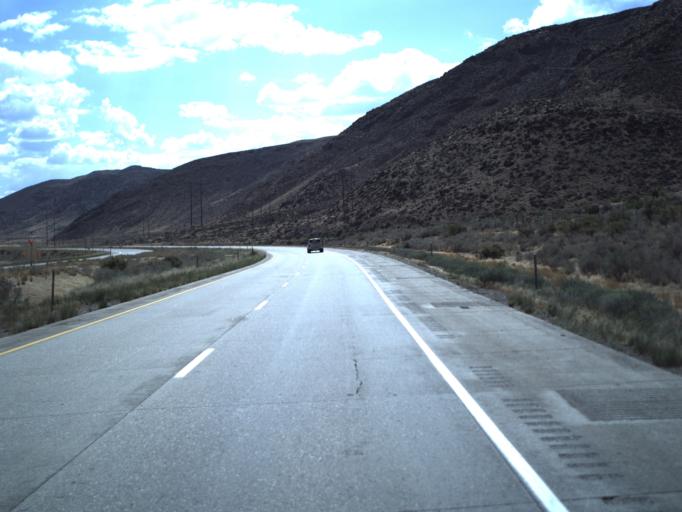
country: US
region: Utah
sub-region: Sevier County
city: Richfield
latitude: 38.7294
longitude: -112.1258
